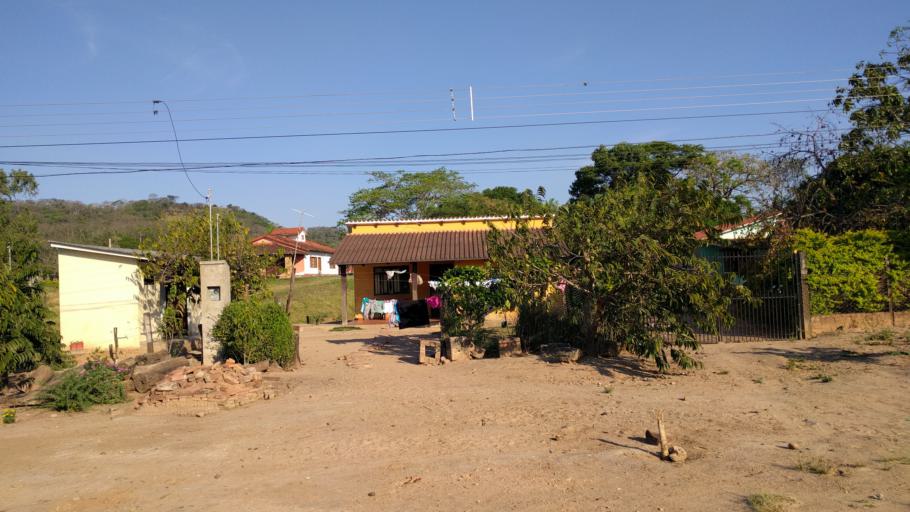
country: BO
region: Santa Cruz
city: Jorochito
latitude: -18.0973
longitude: -63.4512
